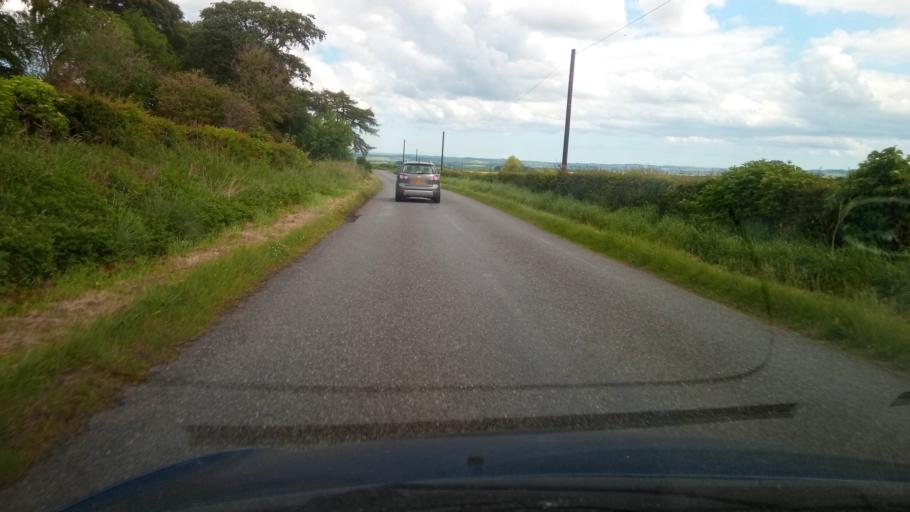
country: GB
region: Scotland
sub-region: The Scottish Borders
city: Coldstream
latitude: 55.6016
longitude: -2.3348
